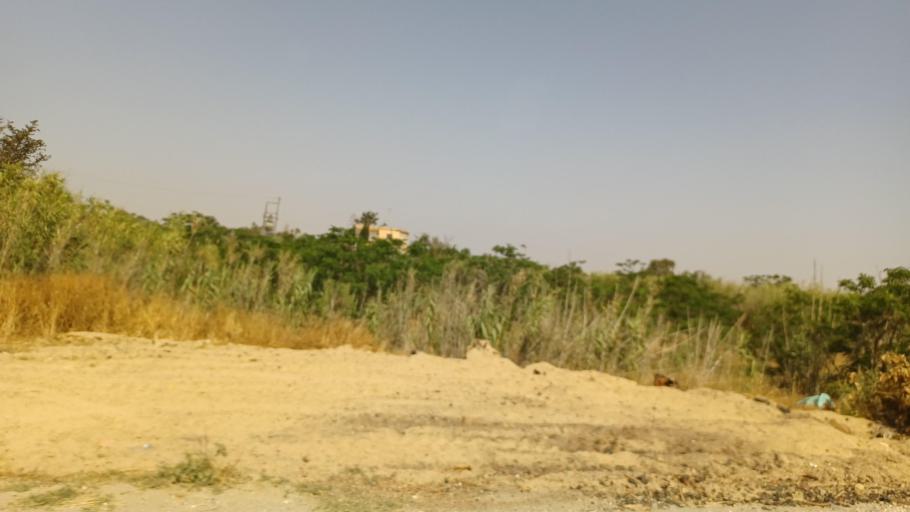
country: CY
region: Ammochostos
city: Avgorou
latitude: 35.0426
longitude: 33.8495
